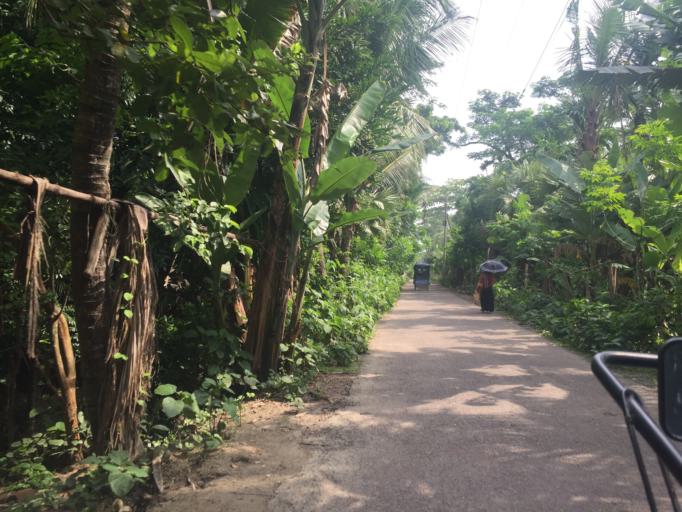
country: BD
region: Barisal
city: Mathba
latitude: 22.2189
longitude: 89.9159
